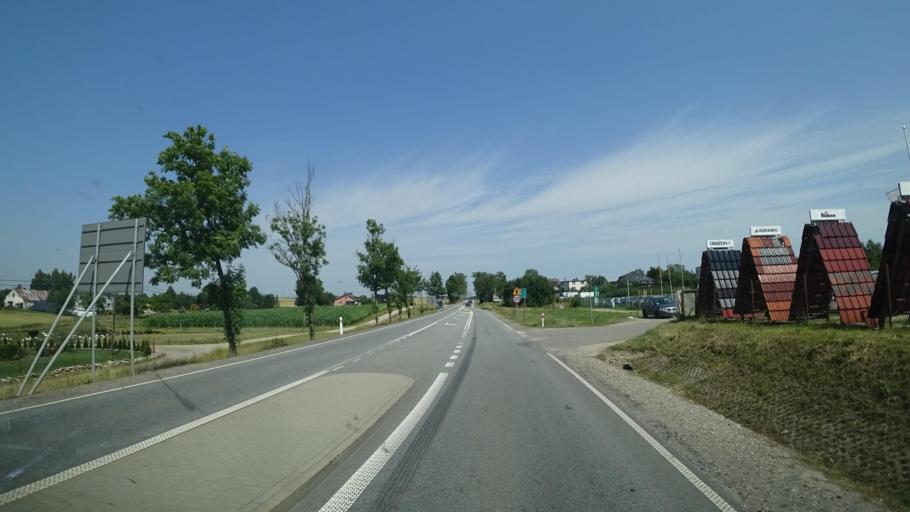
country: PL
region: Pomeranian Voivodeship
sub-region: Powiat koscierski
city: Koscierzyna
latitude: 54.1390
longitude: 18.0170
